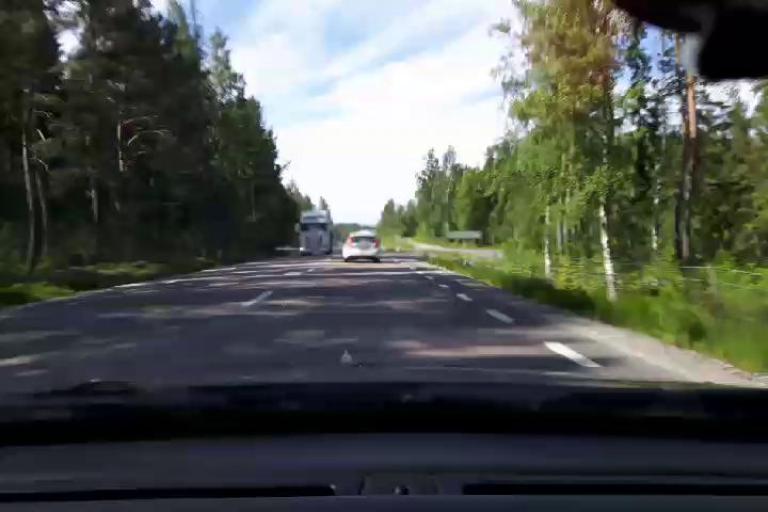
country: SE
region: Gaevleborg
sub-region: Bollnas Kommun
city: Kilafors
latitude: 61.2791
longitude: 16.5223
